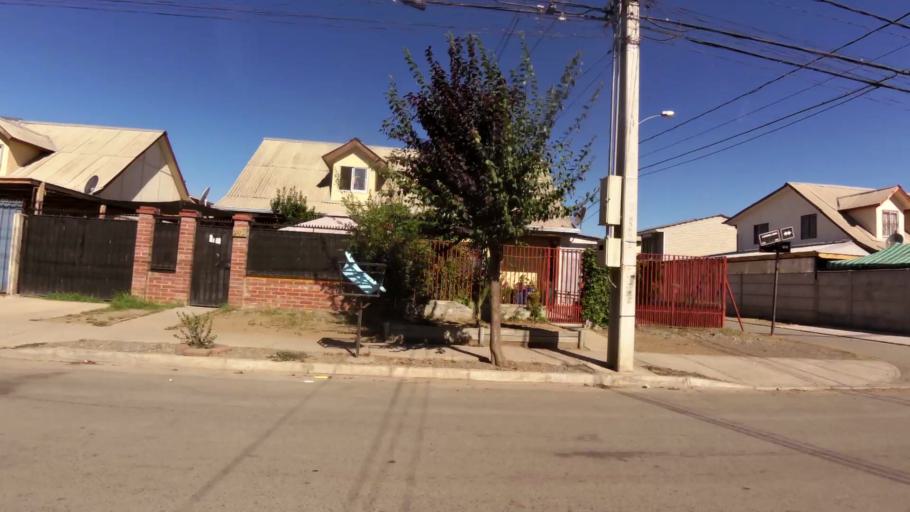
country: CL
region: O'Higgins
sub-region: Provincia de Colchagua
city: Chimbarongo
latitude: -34.5780
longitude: -71.0071
